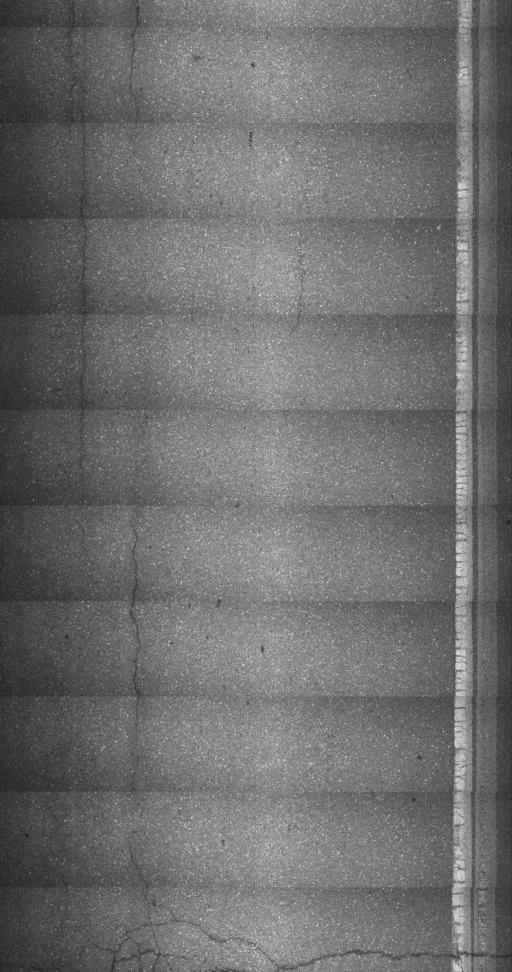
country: US
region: Vermont
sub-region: Orleans County
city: Newport
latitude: 44.9955
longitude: -72.1061
